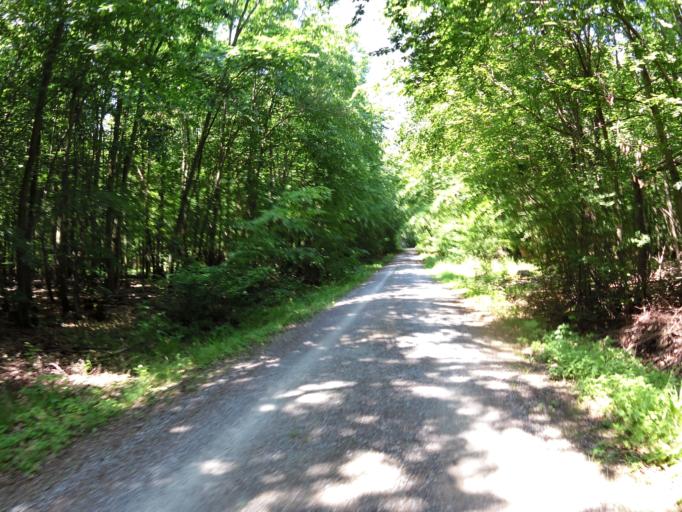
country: DE
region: Bavaria
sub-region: Regierungsbezirk Unterfranken
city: Kist
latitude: 49.7302
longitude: 9.8661
